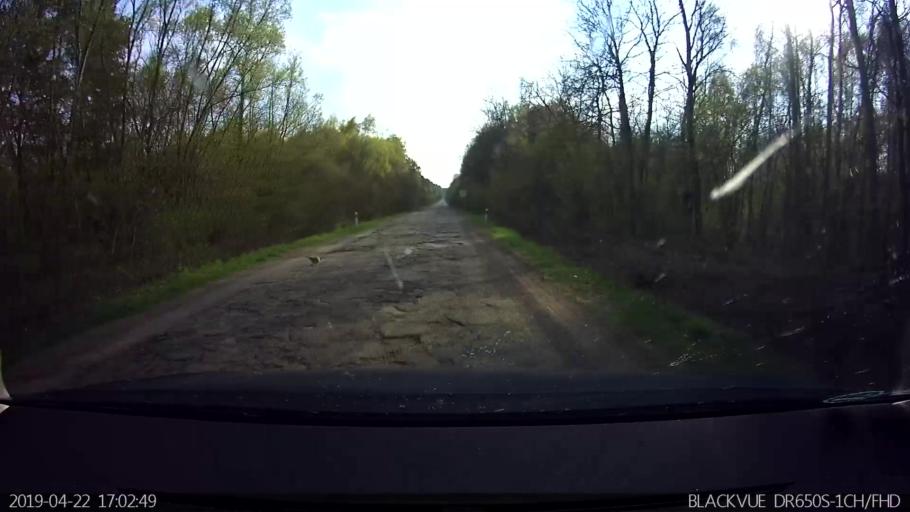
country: PL
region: Podlasie
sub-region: Powiat siemiatycki
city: Drohiczyn
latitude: 52.4229
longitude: 22.6991
